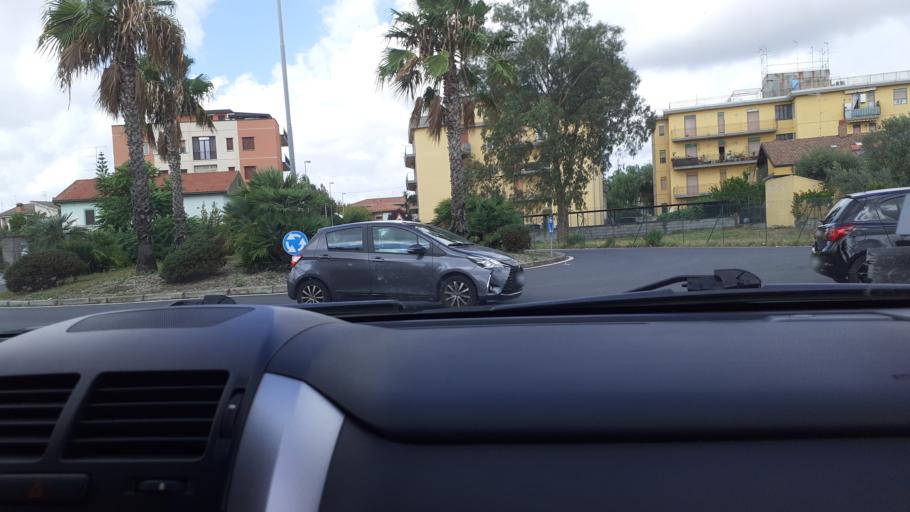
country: IT
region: Sicily
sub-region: Catania
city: San Giovanni la Punta
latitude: 37.5731
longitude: 15.1020
